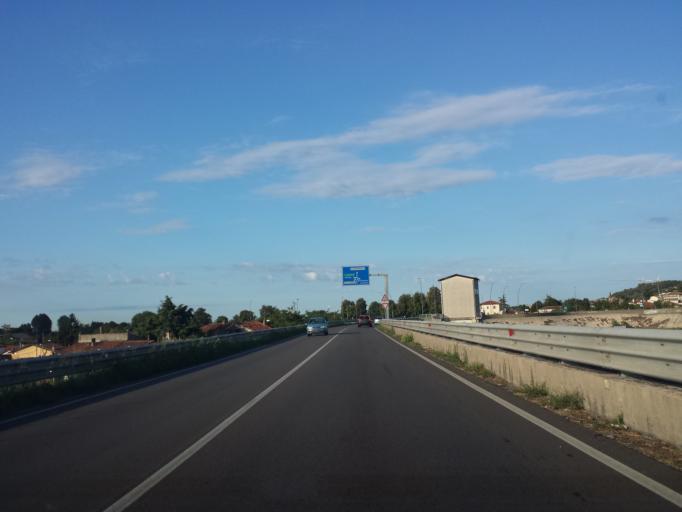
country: IT
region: Veneto
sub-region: Provincia di Vicenza
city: Montebello Vicentino
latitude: 45.4588
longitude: 11.3929
